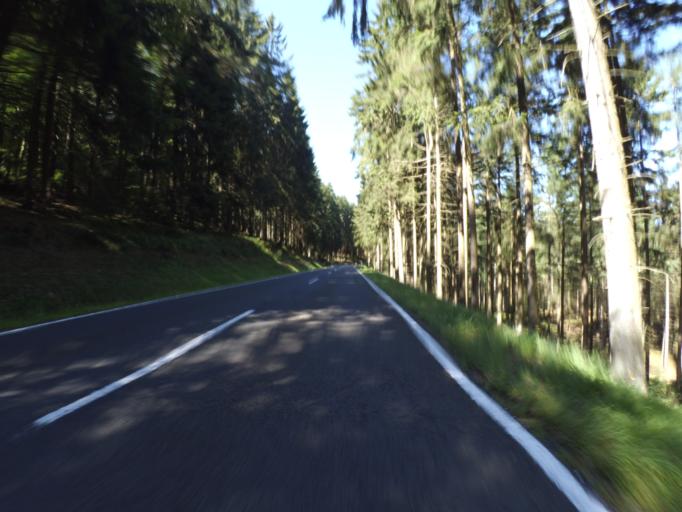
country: DE
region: Rheinland-Pfalz
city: Deudesfeld
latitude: 50.0823
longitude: 6.7319
